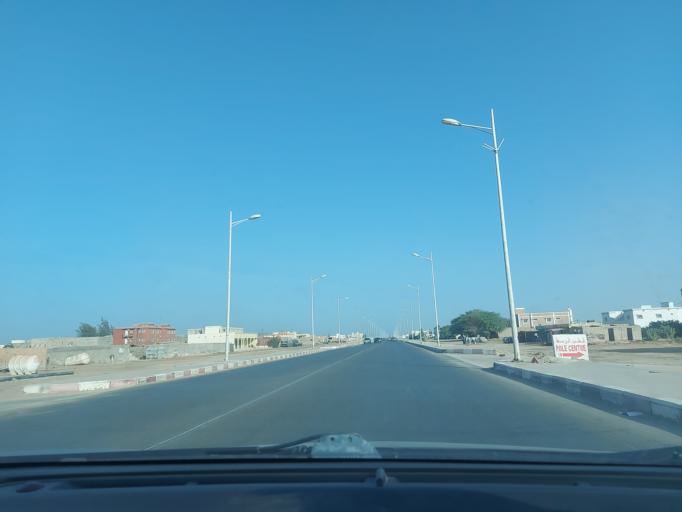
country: MR
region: Nouakchott
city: Nouakchott
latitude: 18.0902
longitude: -16.0083
